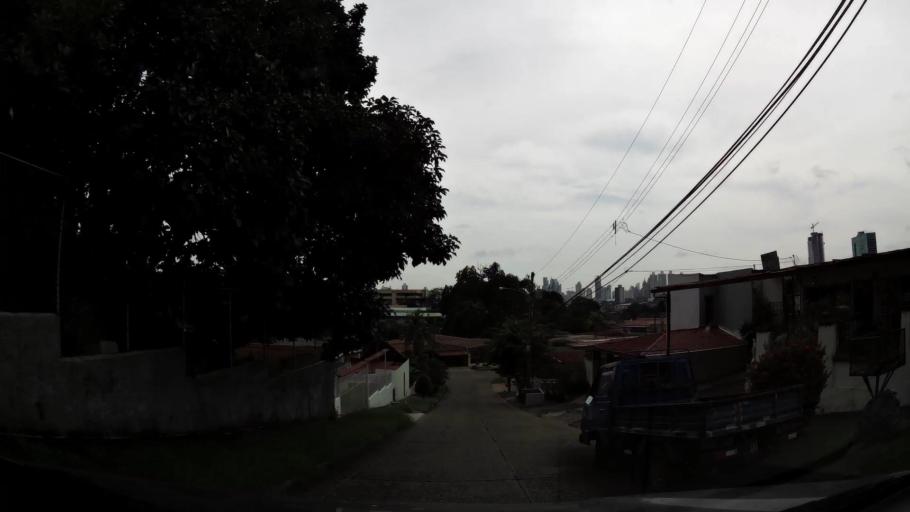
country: PA
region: Panama
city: Panama
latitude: 9.0087
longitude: -79.5292
